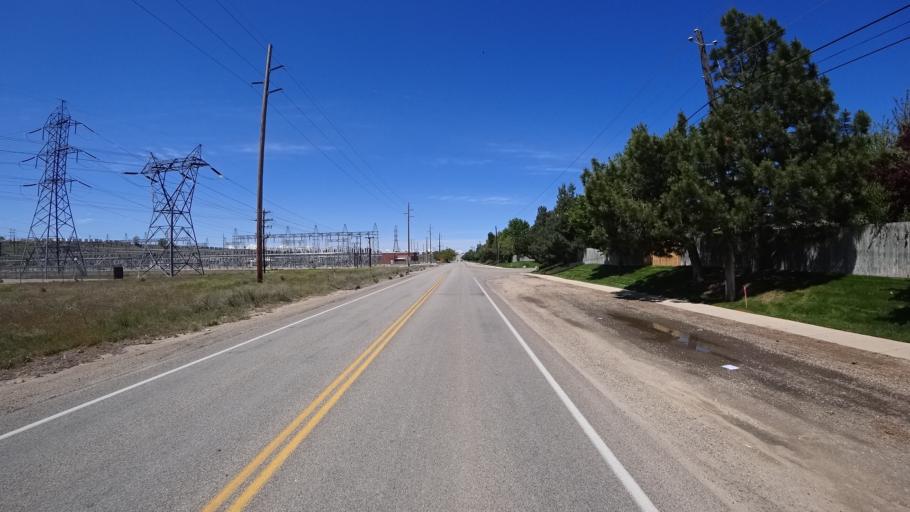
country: US
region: Idaho
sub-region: Ada County
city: Boise
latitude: 43.5605
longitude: -116.1548
